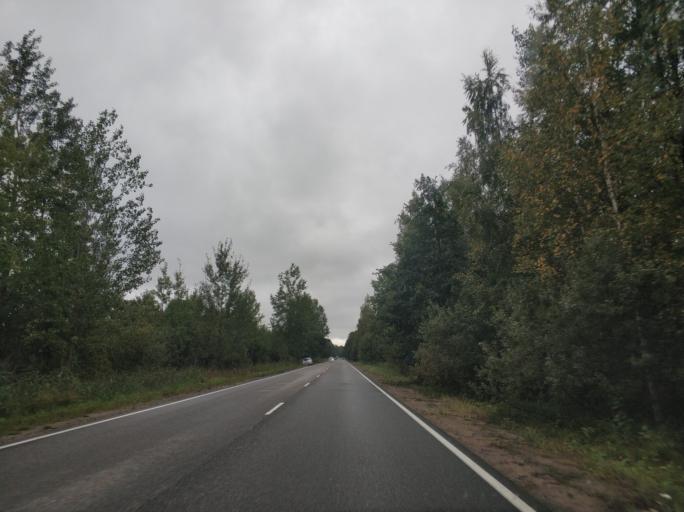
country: RU
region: Leningrad
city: Borisova Griva
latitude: 60.1401
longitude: 30.9525
